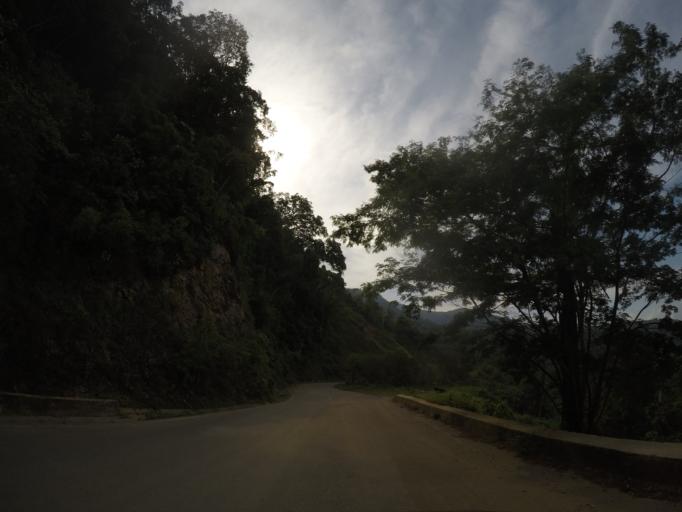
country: MX
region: Oaxaca
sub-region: San Pedro Pochutla
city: Los Naranjos Esquipulas
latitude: 15.9582
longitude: -96.4541
